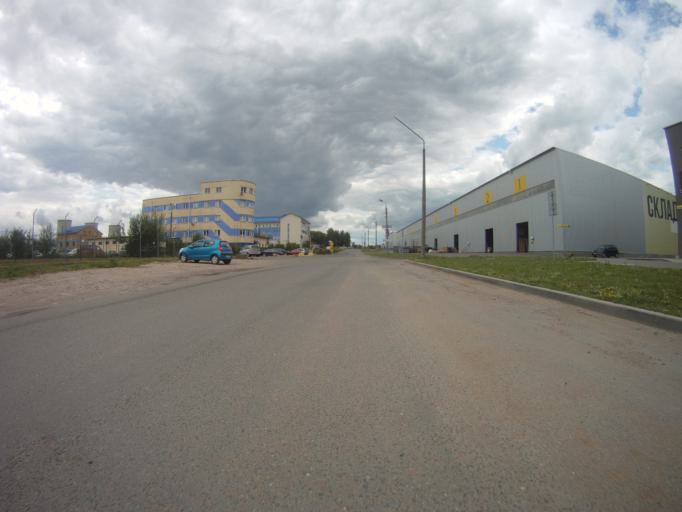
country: BY
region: Minsk
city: Malinovka
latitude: 53.8767
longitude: 27.4158
